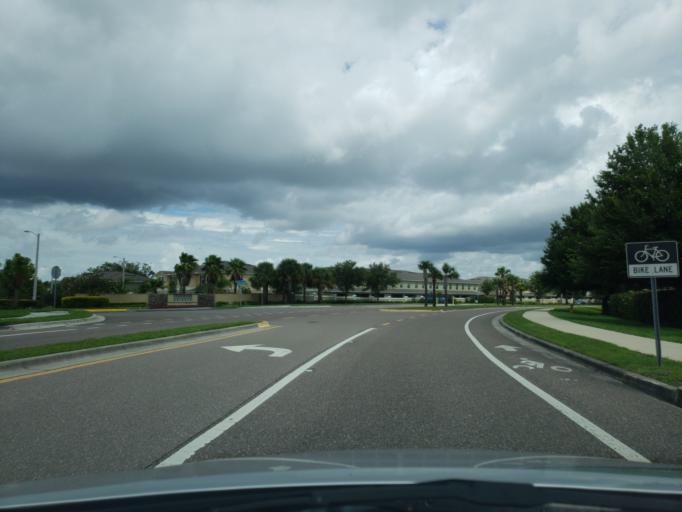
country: US
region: Florida
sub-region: Hillsborough County
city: Progress Village
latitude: 27.9148
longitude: -82.3304
